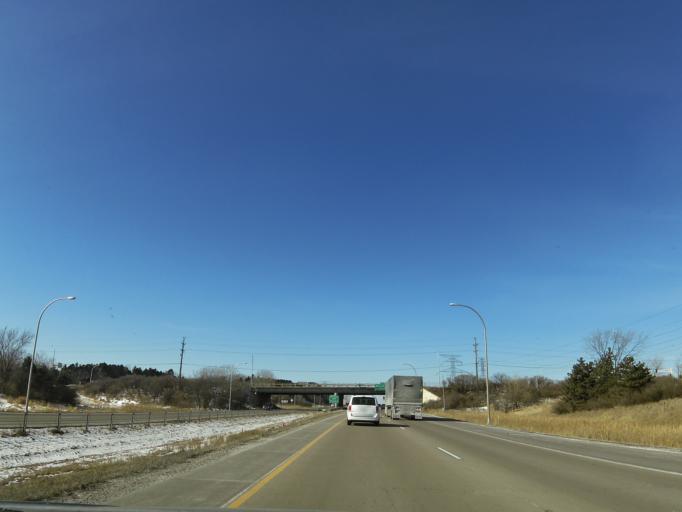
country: US
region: Minnesota
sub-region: Ramsey County
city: North Saint Paul
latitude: 45.0340
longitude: -92.9825
